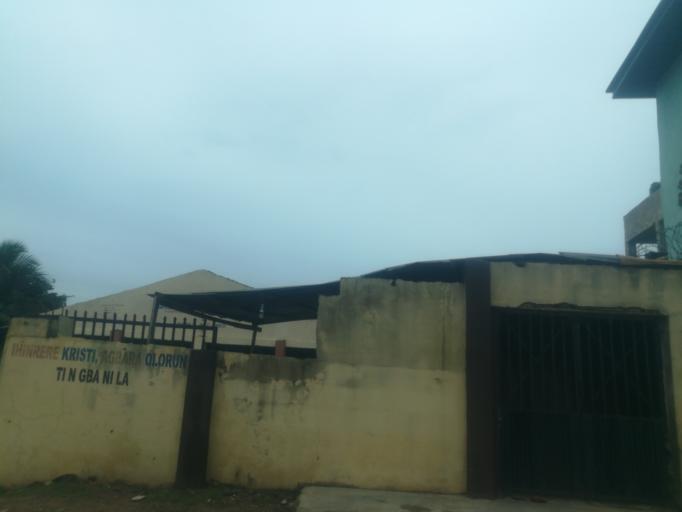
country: NG
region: Oyo
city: Ibadan
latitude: 7.3347
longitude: 3.8923
